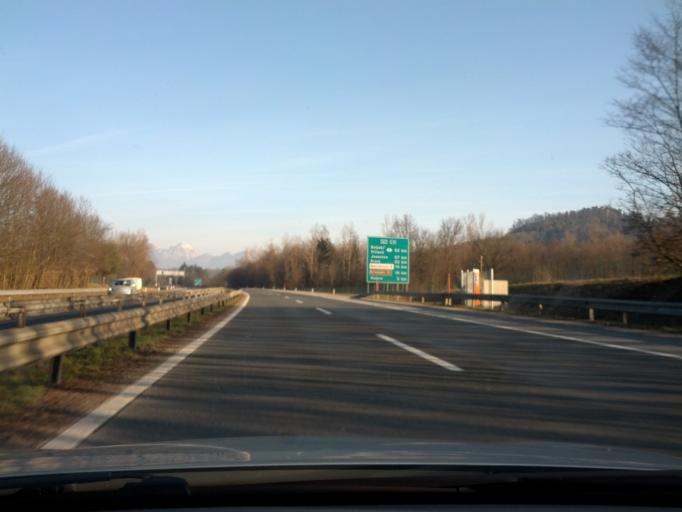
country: SI
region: Medvode
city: Zgornje Pirnice
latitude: 46.1287
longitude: 14.4824
